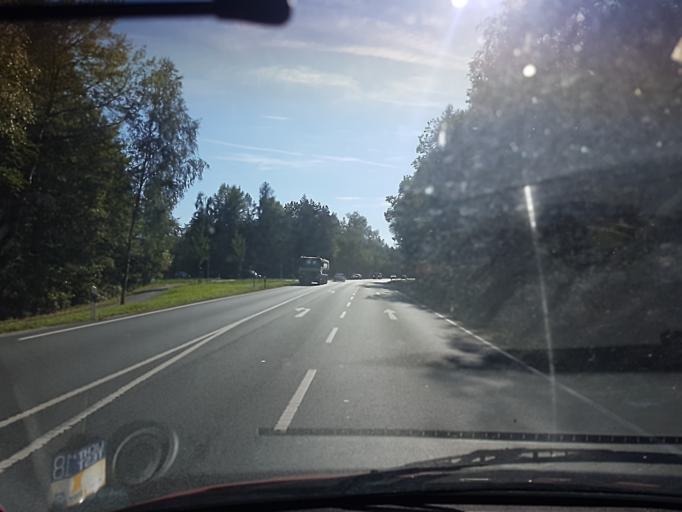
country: DE
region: Bavaria
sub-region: Regierungsbezirk Mittelfranken
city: Hemhofen
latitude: 49.7012
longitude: 10.9487
